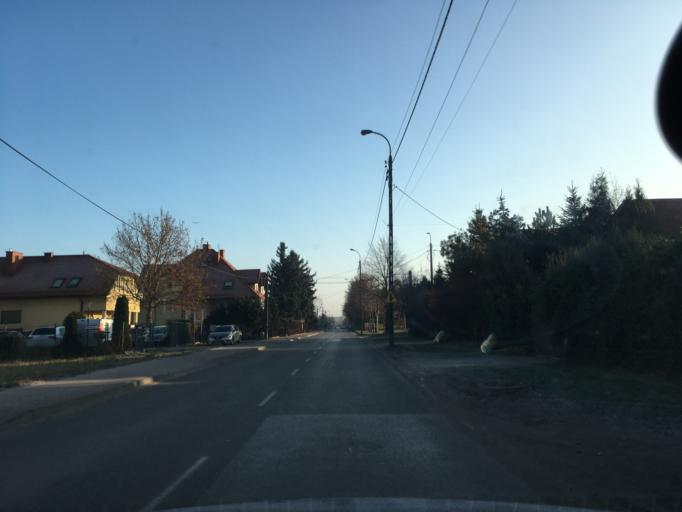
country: PL
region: Masovian Voivodeship
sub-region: Powiat piaseczynski
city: Piaseczno
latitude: 52.0707
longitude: 21.0037
